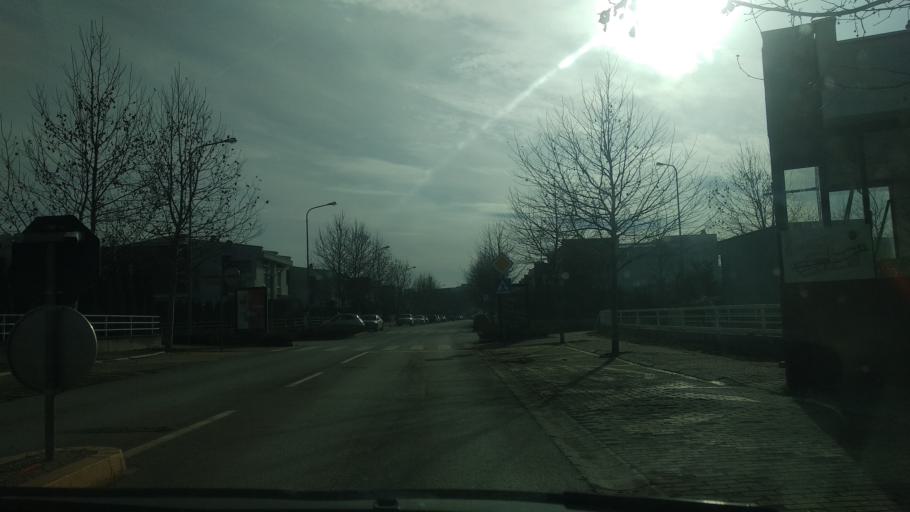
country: XK
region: Pristina
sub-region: Komuna e Gracanices
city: Glanica
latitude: 42.5884
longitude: 21.1078
